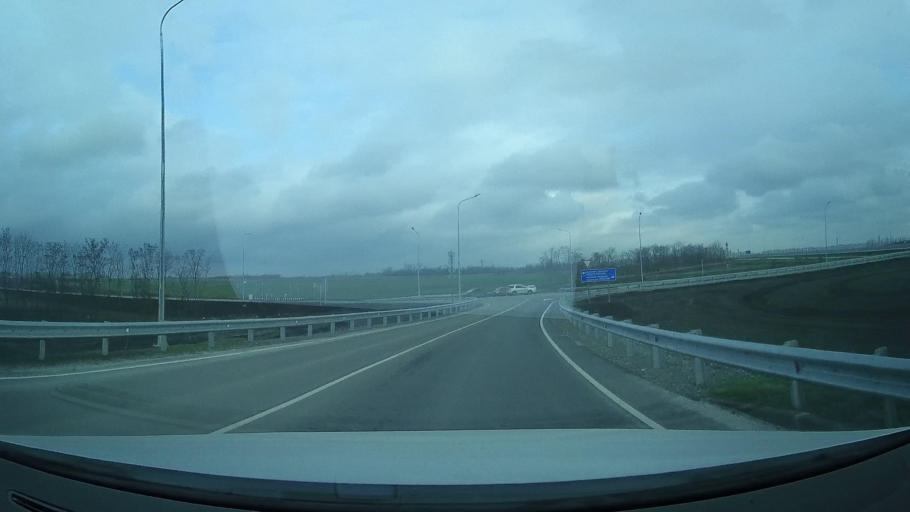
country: RU
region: Rostov
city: Grushevskaya
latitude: 47.4947
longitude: 39.9513
